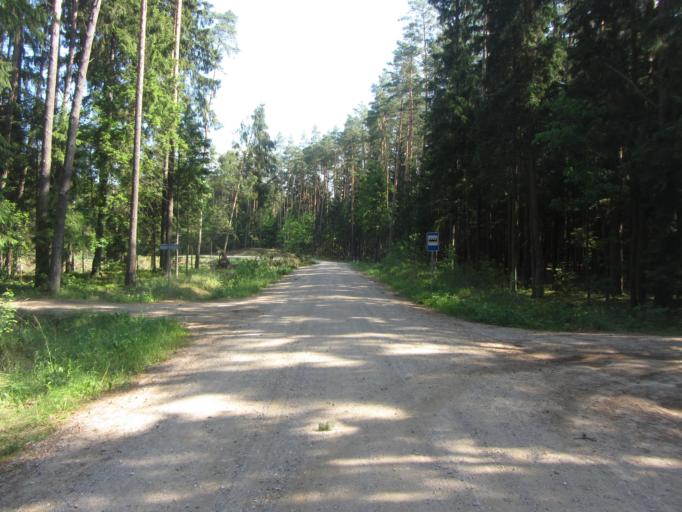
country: LT
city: Prienai
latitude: 54.5542
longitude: 23.9594
